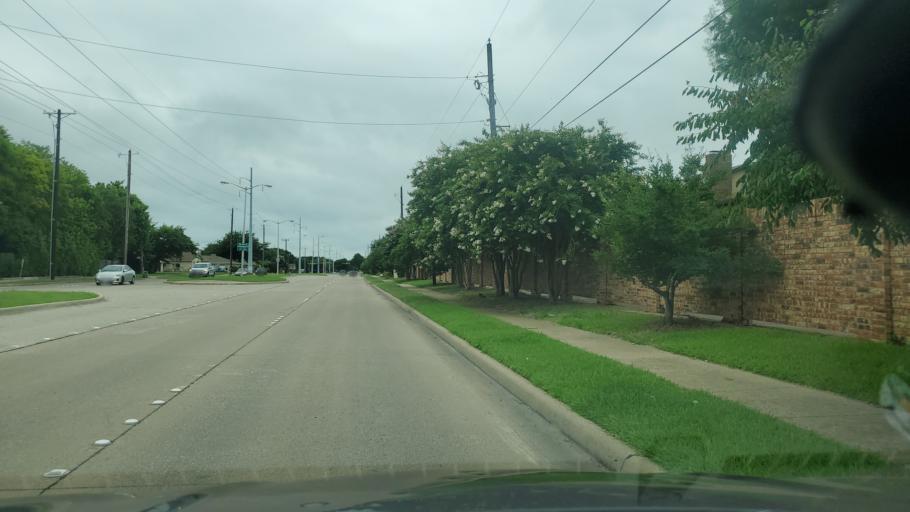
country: US
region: Texas
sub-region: Dallas County
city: Garland
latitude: 32.9422
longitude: -96.6653
